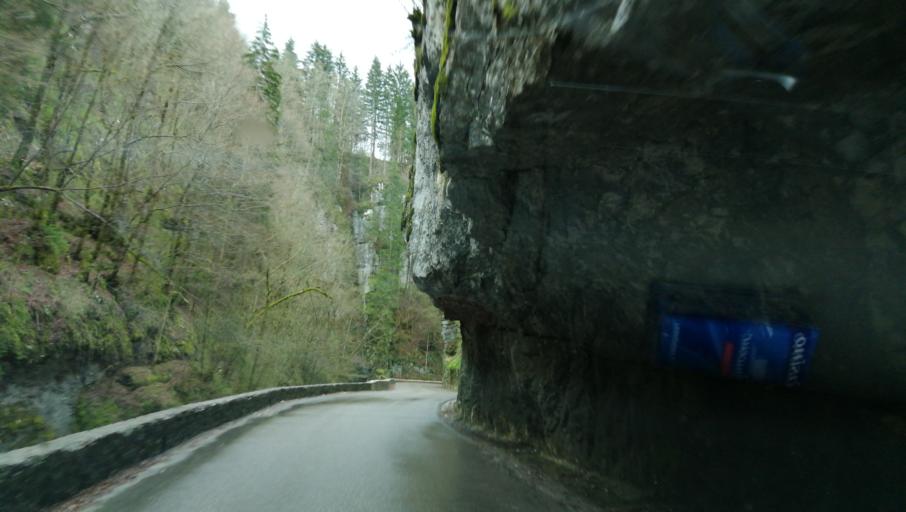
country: FR
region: Rhone-Alpes
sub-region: Departement de l'Isere
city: Villard-de-Lans
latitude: 45.0812
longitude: 5.5212
